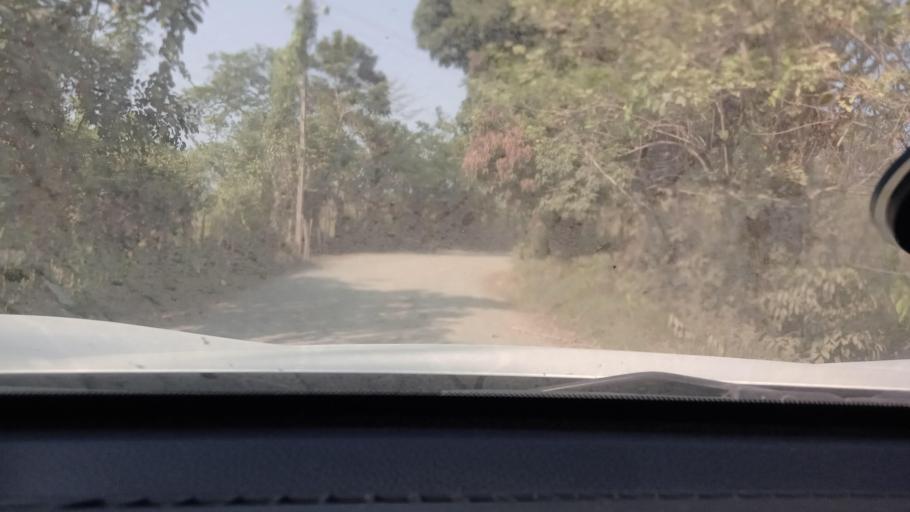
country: MX
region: Tabasco
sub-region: Huimanguillo
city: Francisco Rueda
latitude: 17.6536
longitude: -93.8885
